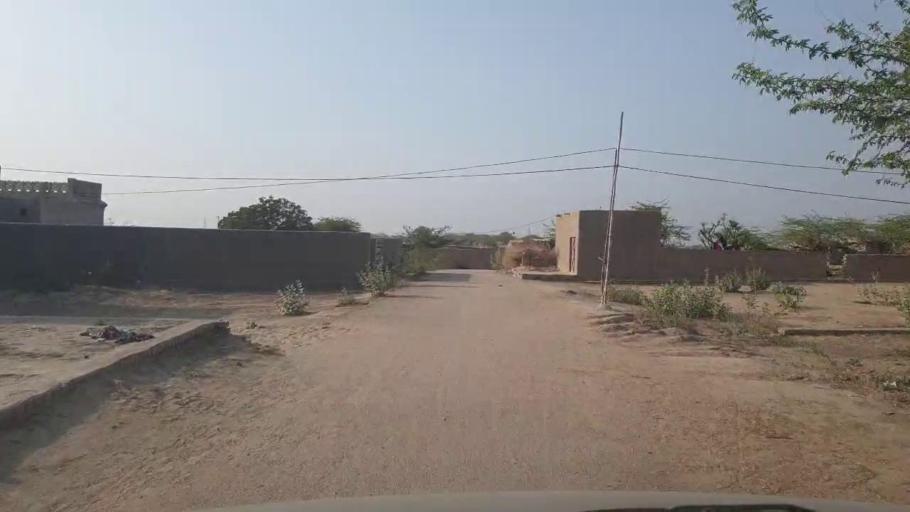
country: PK
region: Sindh
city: Umarkot
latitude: 25.3555
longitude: 69.7552
